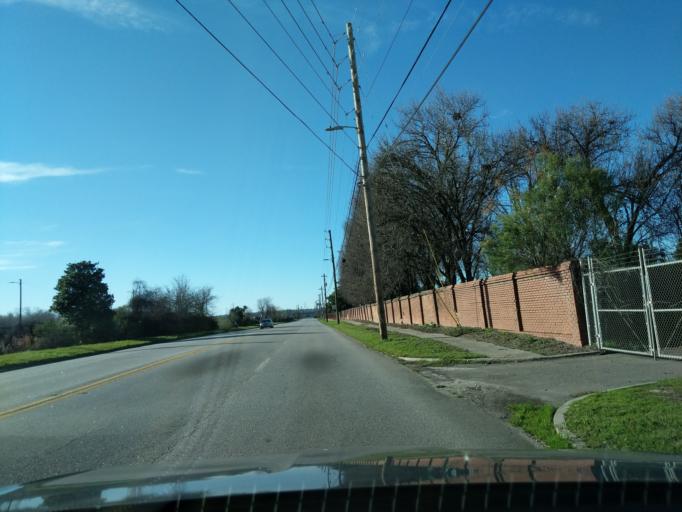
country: US
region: Georgia
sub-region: Richmond County
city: Augusta
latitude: 33.4579
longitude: -81.9574
